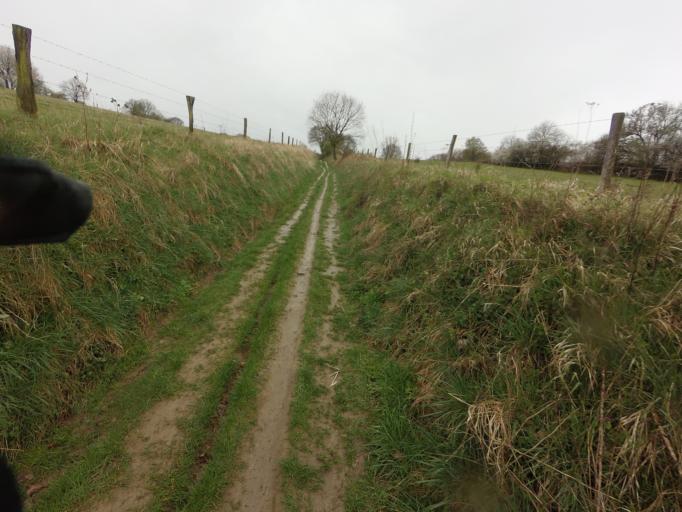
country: NL
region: Limburg
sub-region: Valkenburg aan de Geul
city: Schin op Geul
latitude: 50.8428
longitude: 5.8613
